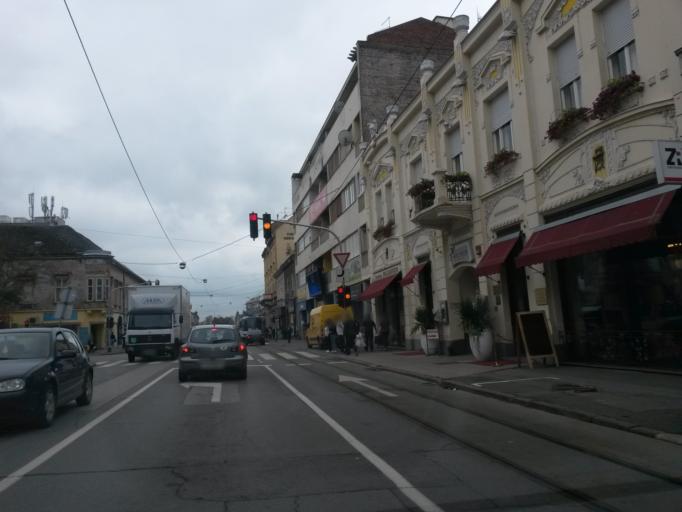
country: HR
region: Osjecko-Baranjska
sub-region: Grad Osijek
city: Osijek
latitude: 45.5588
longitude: 18.6760
